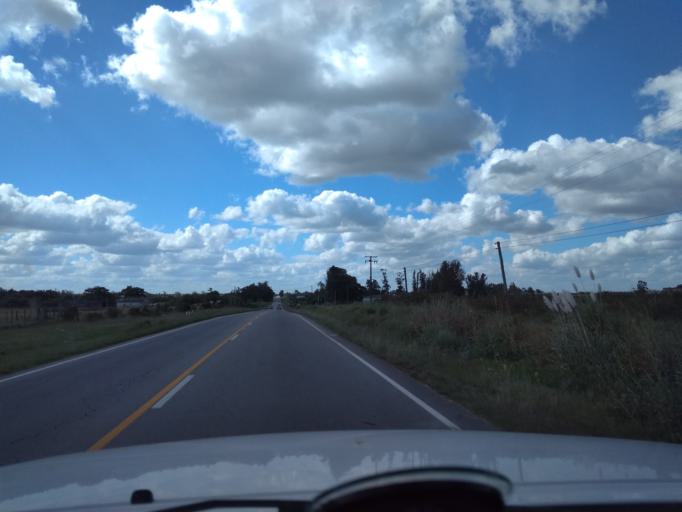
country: UY
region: Canelones
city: Joaquin Suarez
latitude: -34.7021
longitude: -56.0574
